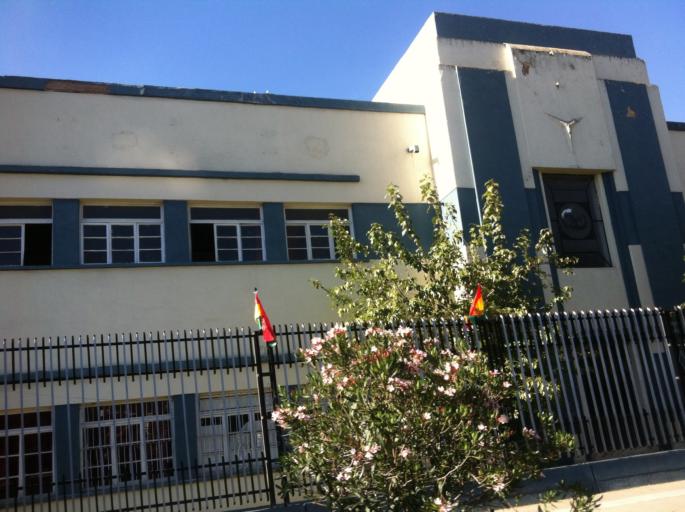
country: BO
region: Cochabamba
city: Cochabamba
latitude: -17.3790
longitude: -66.1429
